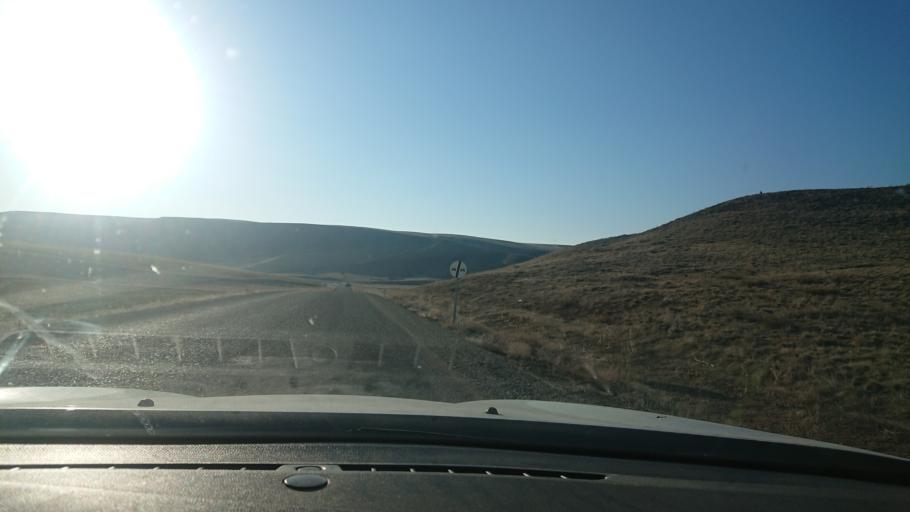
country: TR
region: Aksaray
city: Acipinar
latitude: 38.7113
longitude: 33.7671
